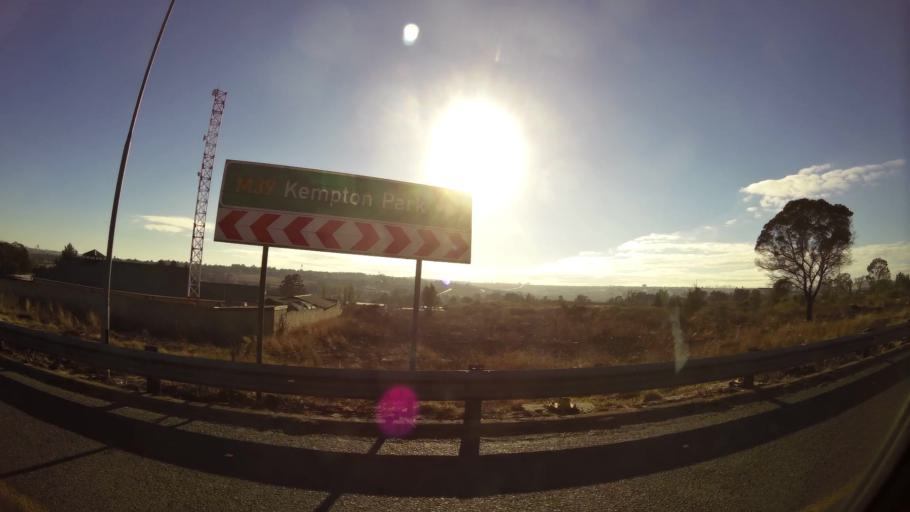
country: ZA
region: Gauteng
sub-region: City of Johannesburg Metropolitan Municipality
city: Midrand
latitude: -26.0368
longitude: 28.1421
